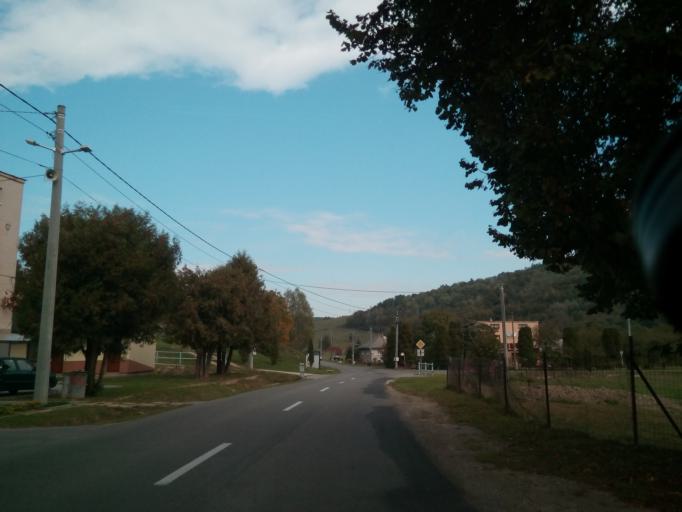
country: SK
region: Presovsky
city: Svidnik
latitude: 49.2562
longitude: 21.4483
